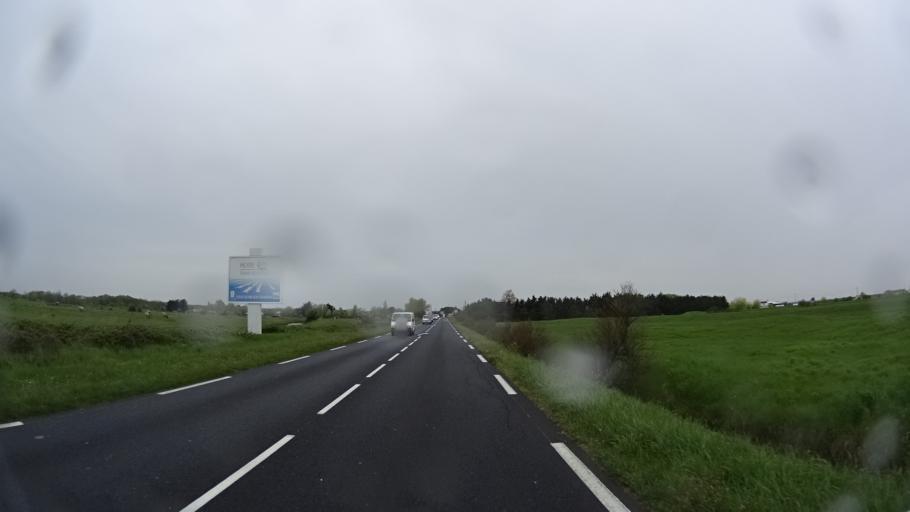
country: FR
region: Pays de la Loire
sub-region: Departement de la Vendee
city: La Barre-de-Monts
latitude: 46.8895
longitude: -2.1061
